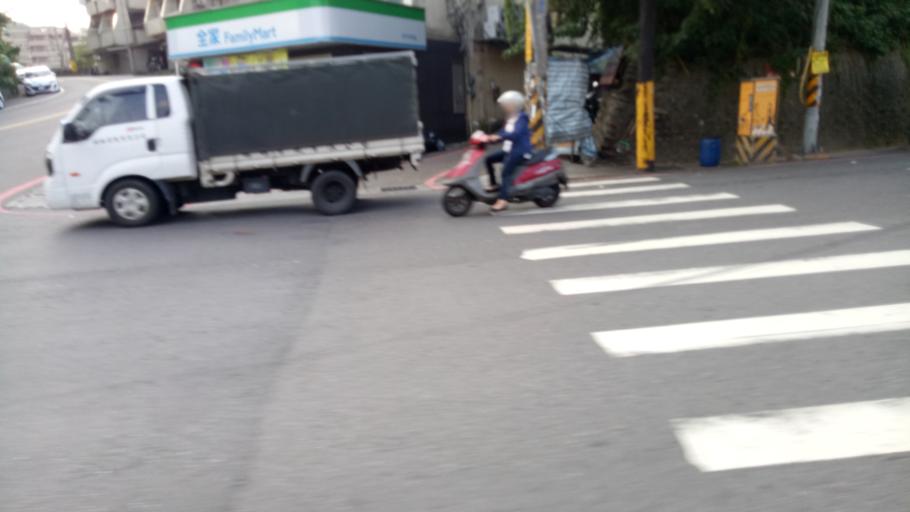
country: TW
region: Taiwan
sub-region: Hsinchu
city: Hsinchu
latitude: 24.7749
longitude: 120.9671
